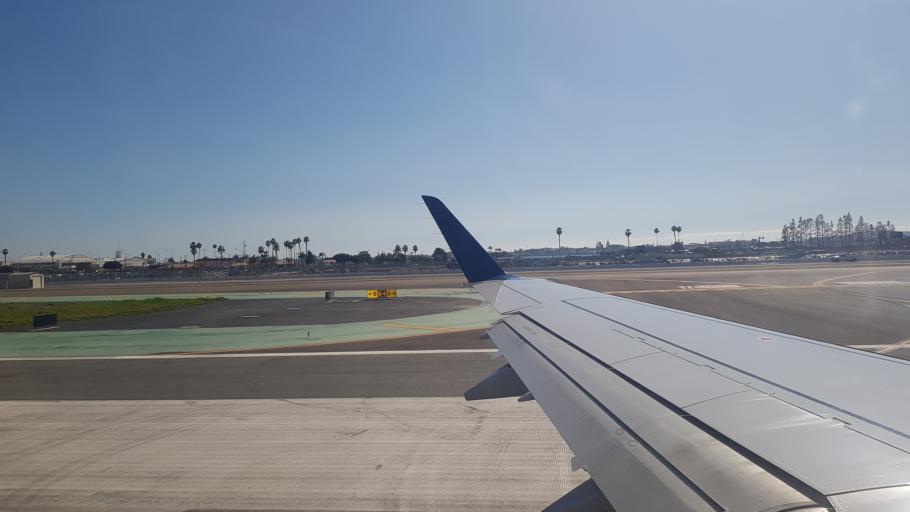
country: US
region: California
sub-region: San Diego County
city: San Diego
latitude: 32.7321
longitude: -117.1833
